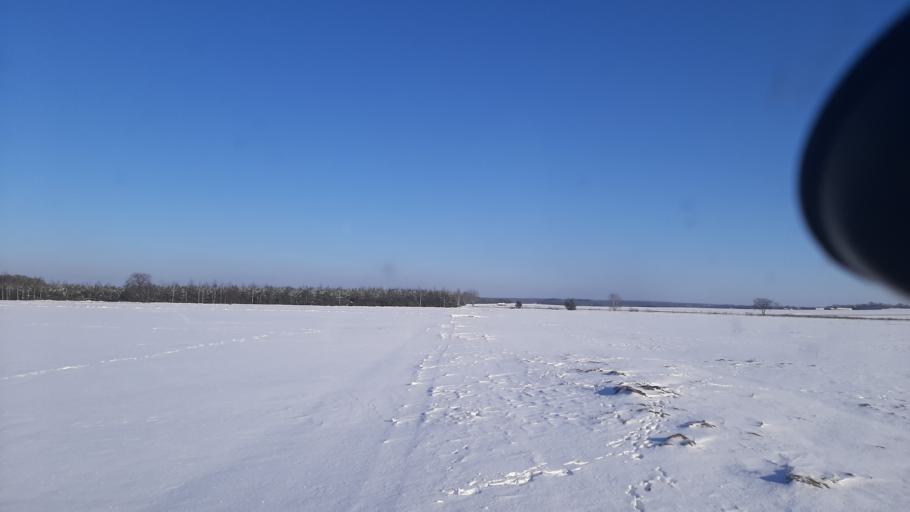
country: PL
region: Lublin Voivodeship
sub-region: Powiat lubelski
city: Jastkow
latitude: 51.3728
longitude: 22.4351
